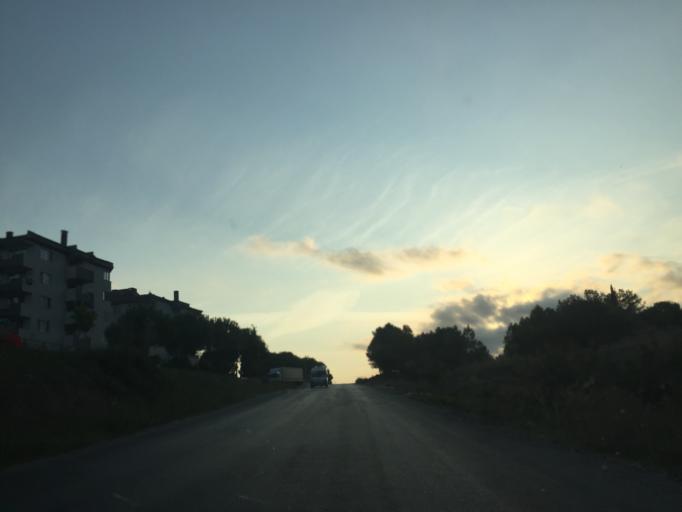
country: TR
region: Balikesir
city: Gonen
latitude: 40.0916
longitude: 27.6467
